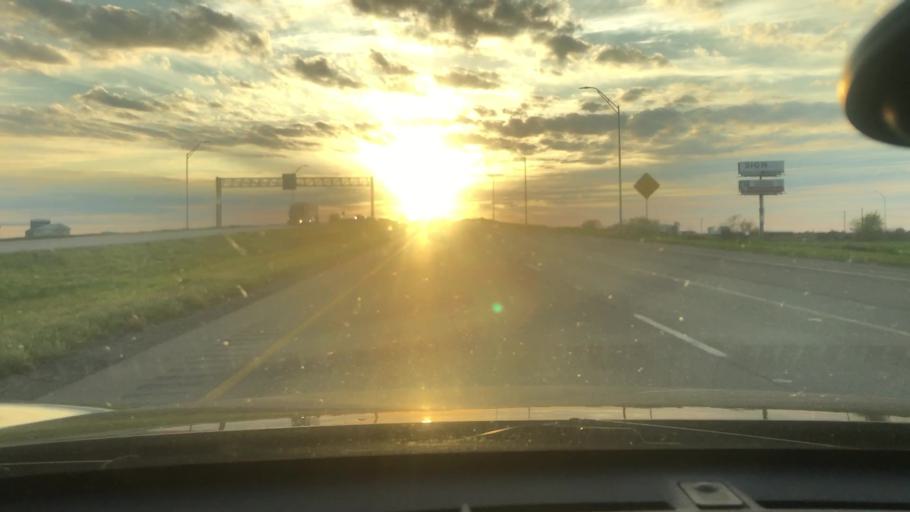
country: US
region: Texas
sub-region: Wharton County
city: El Campo
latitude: 29.1746
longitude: -96.2987
